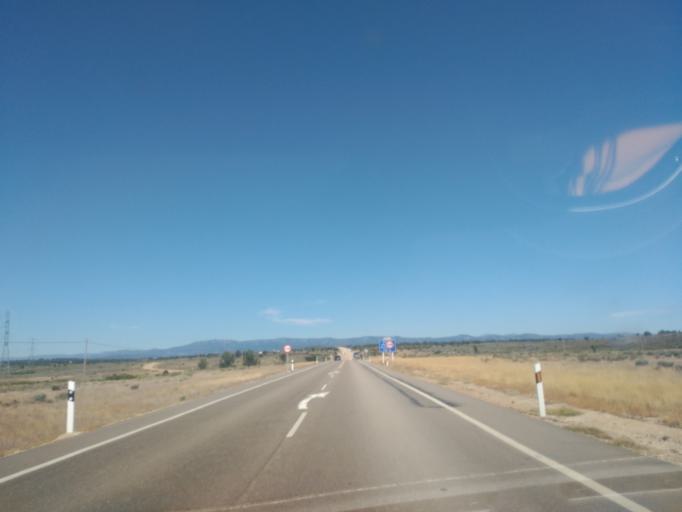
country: ES
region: Castille and Leon
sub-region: Provincia de Zamora
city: Villardeciervos
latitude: 41.9966
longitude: -6.2472
